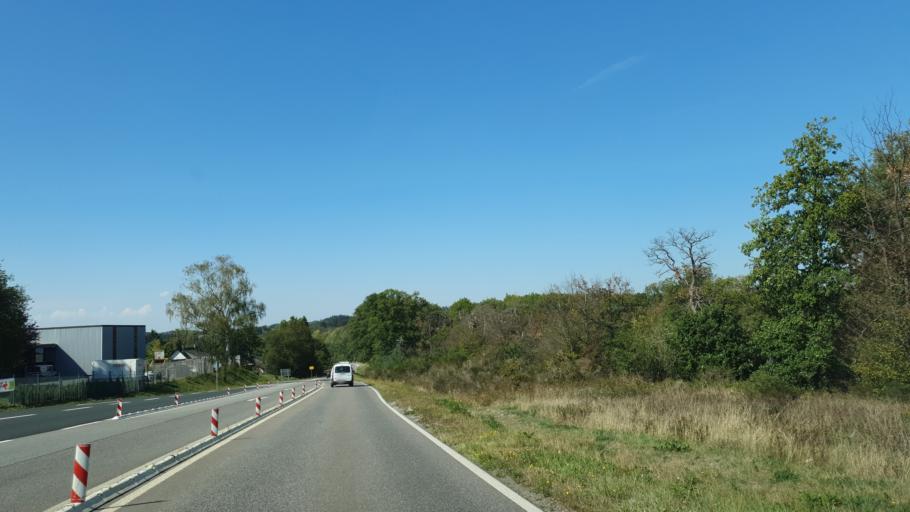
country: DE
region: Rheinland-Pfalz
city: Kratzenburg
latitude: 50.2154
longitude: 7.5422
